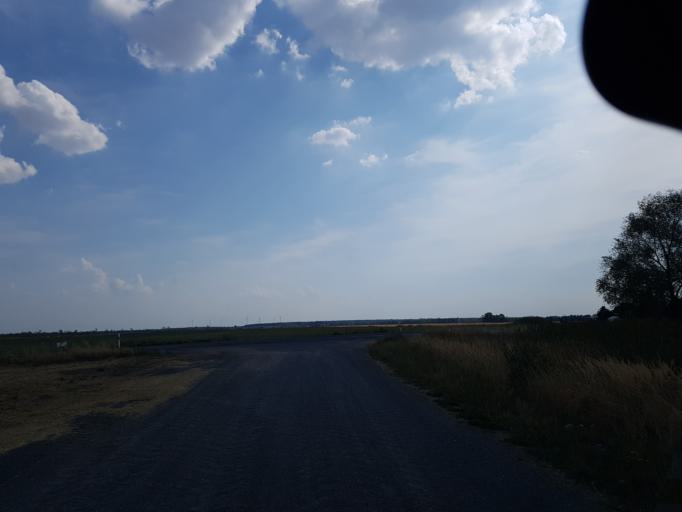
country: DE
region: Brandenburg
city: Treuenbrietzen
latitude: 51.9904
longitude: 12.8684
